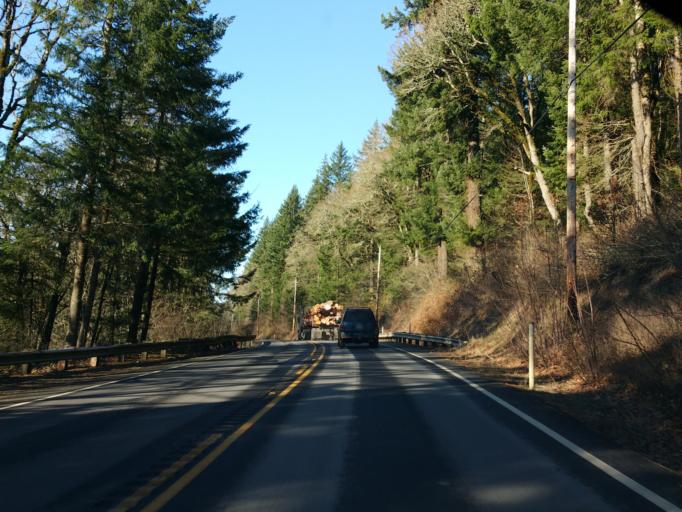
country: US
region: Washington
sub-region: Clark County
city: Washougal
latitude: 45.5651
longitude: -122.2772
